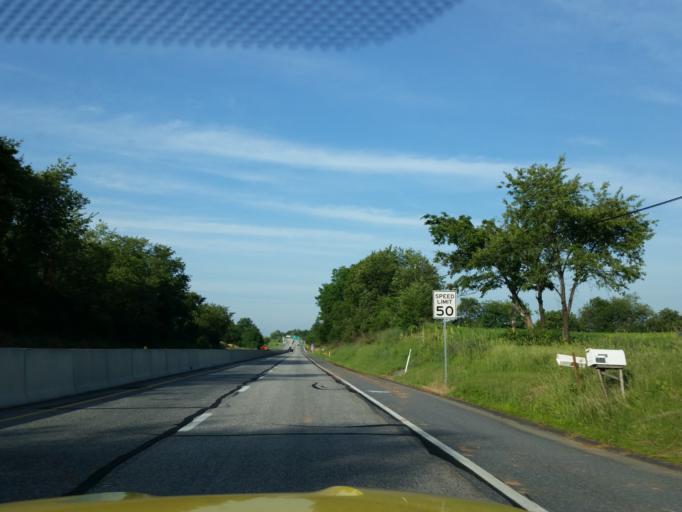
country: US
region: Pennsylvania
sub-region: Lebanon County
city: Fredericksburg
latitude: 40.4507
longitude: -76.3953
